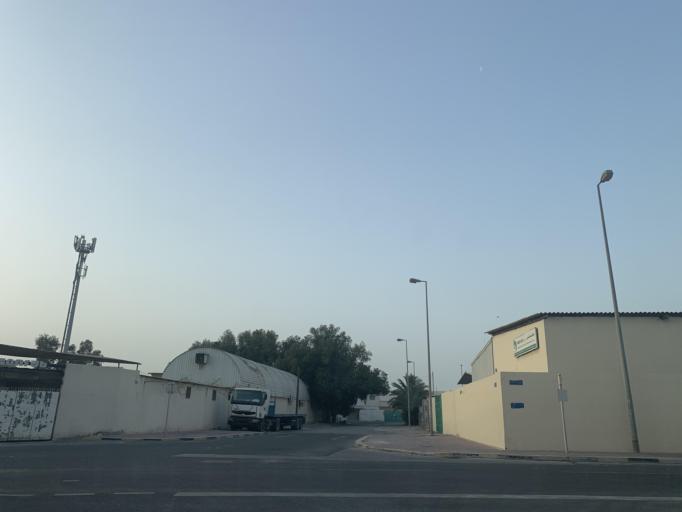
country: BH
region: Manama
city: Manama
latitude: 26.1983
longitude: 50.5942
